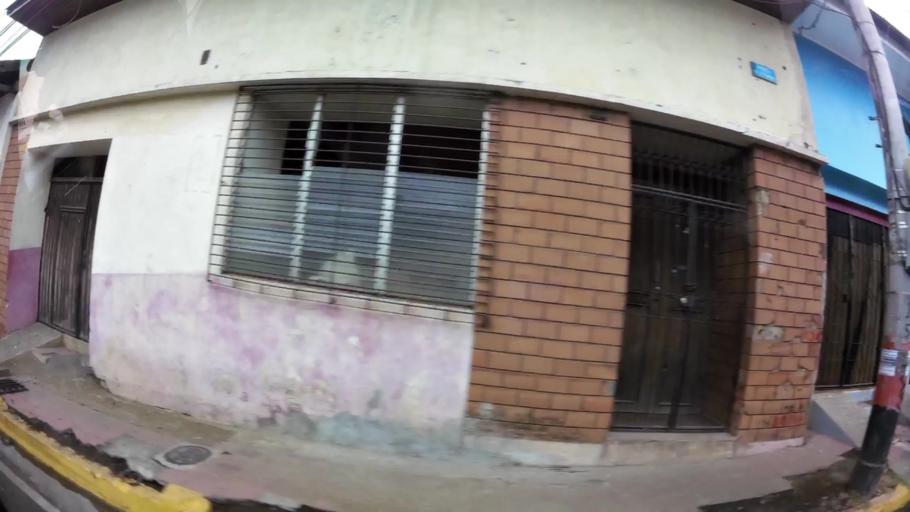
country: NI
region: Leon
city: Leon
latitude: 12.4330
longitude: -86.8804
